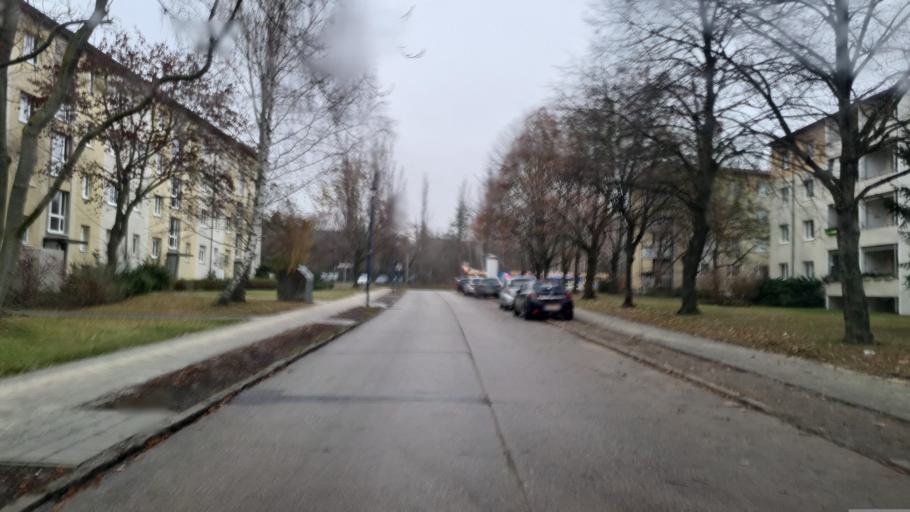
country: DE
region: Brandenburg
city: Cottbus
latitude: 51.7464
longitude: 14.3074
